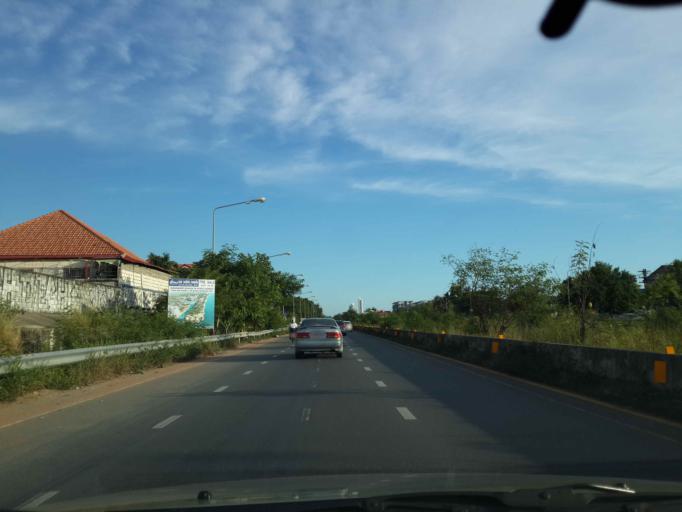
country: TH
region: Chon Buri
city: Phatthaya
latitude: 12.9071
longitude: 100.9014
